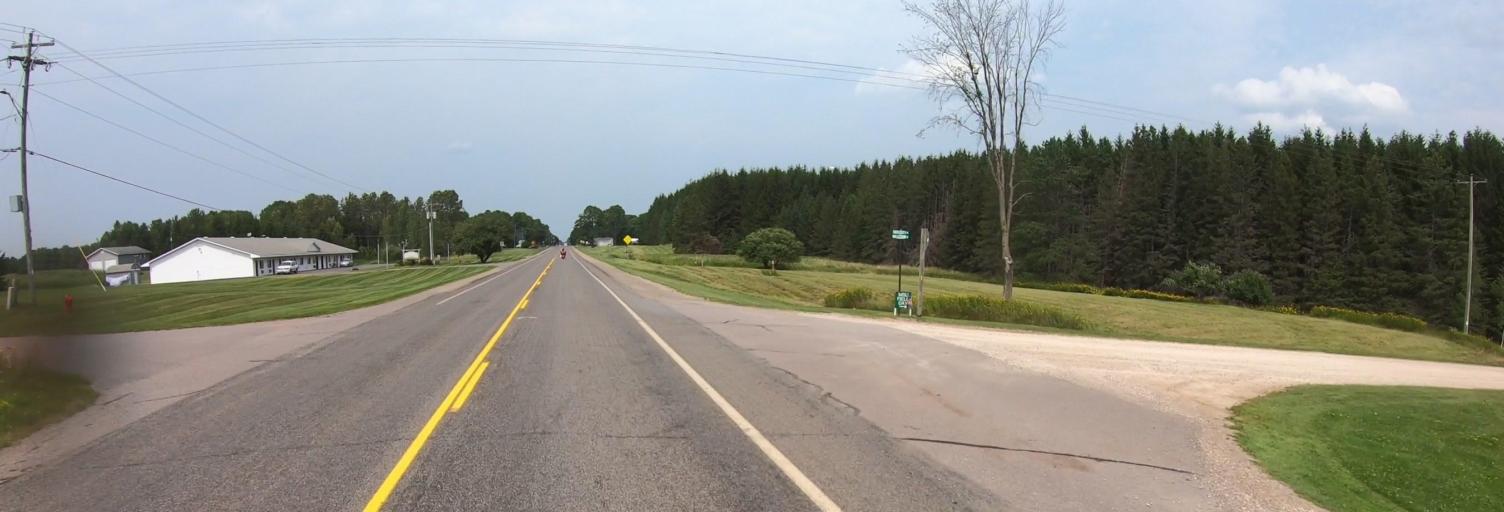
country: US
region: Michigan
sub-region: Alger County
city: Munising
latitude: 46.3403
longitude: -86.9288
